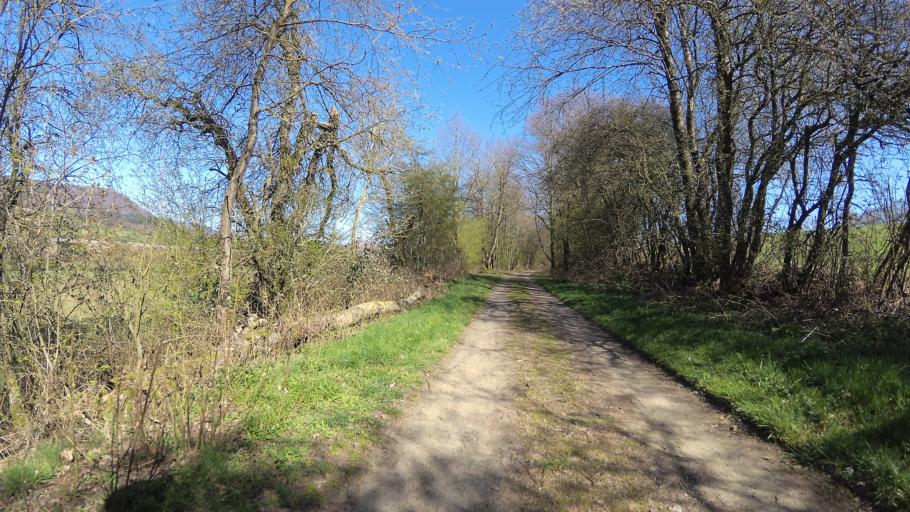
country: DE
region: Rheinland-Pfalz
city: Reichweiler
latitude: 49.5343
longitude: 7.3065
